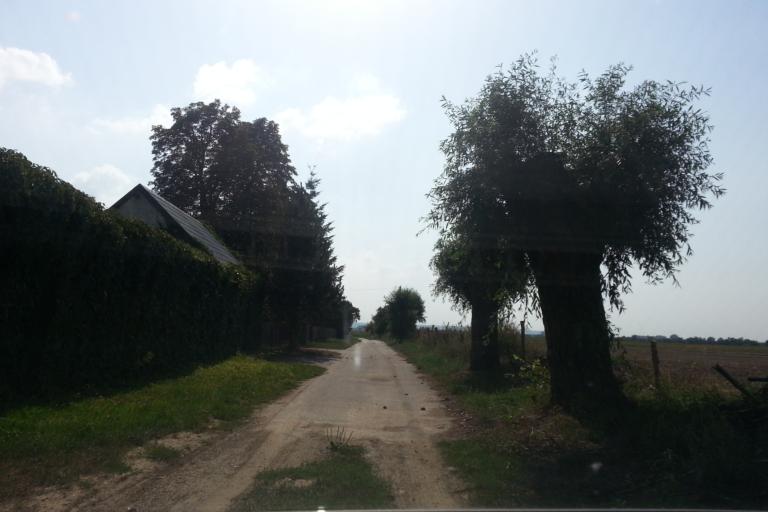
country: DE
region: Mecklenburg-Vorpommern
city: Ferdinandshof
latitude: 53.6275
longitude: 13.8004
